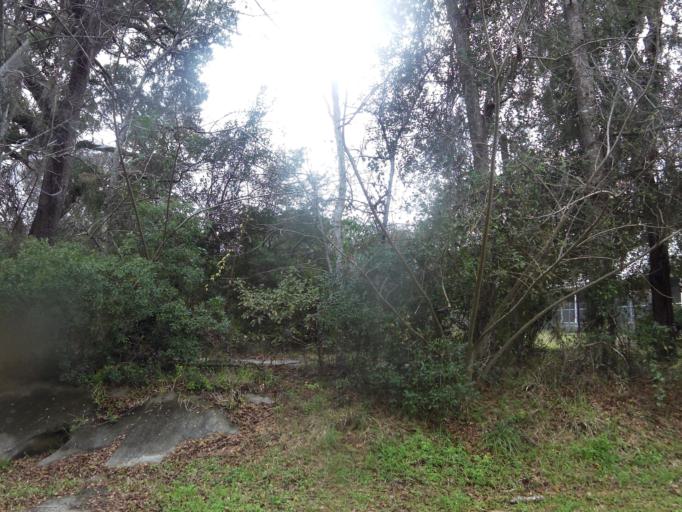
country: US
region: Florida
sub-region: Nassau County
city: Fernandina Beach
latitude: 30.5741
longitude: -81.4491
